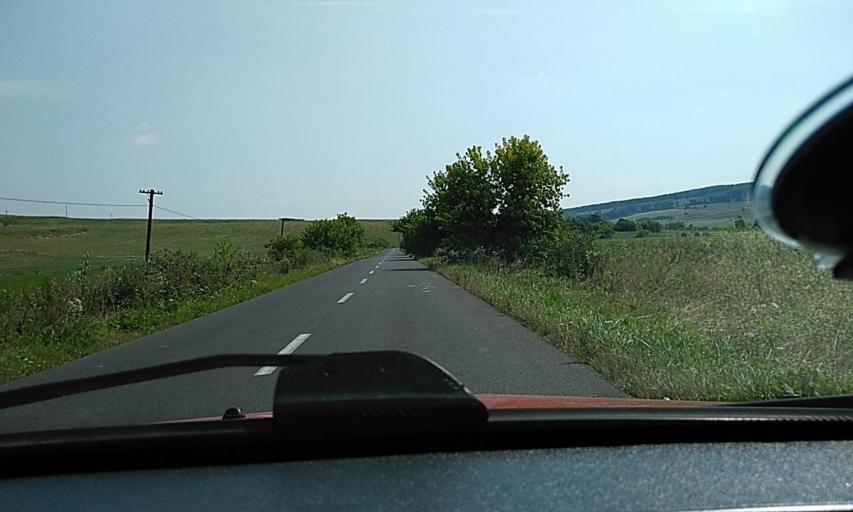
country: RO
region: Brasov
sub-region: Oras Rupea
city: Rupea
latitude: 46.0199
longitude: 25.1832
